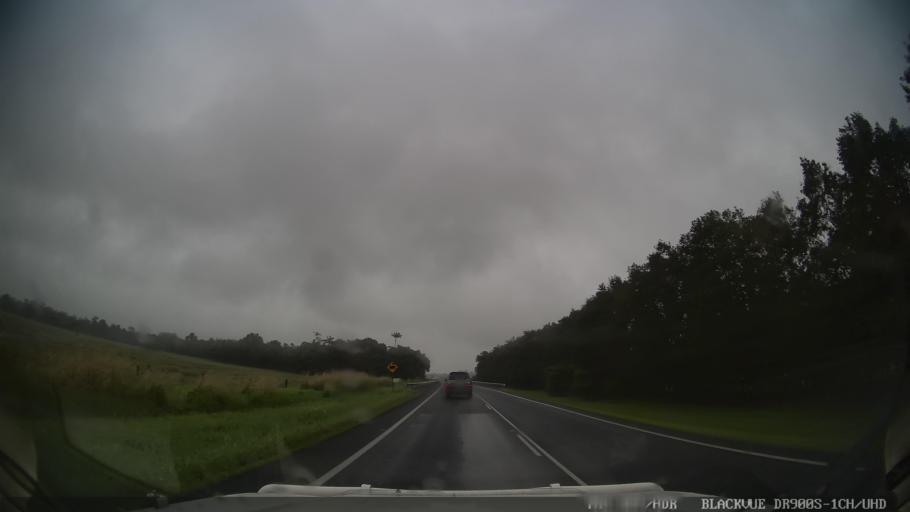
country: AU
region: Queensland
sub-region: Cassowary Coast
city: Innisfail
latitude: -17.6503
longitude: 146.0333
